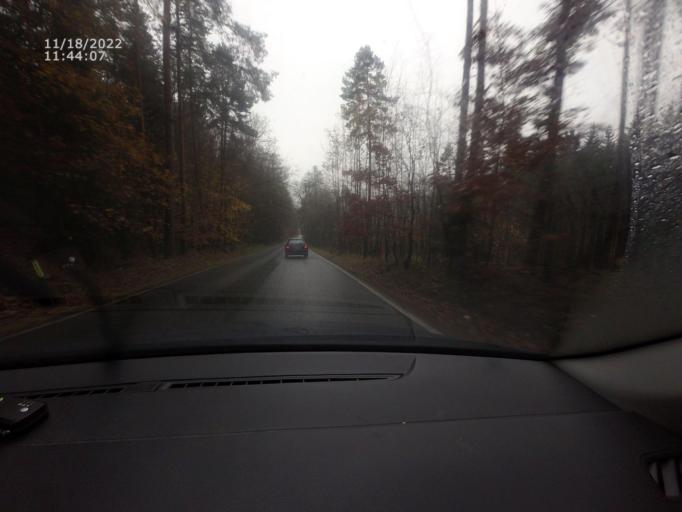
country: CZ
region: Plzensky
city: St'ahlavy
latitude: 49.6851
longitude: 13.5115
